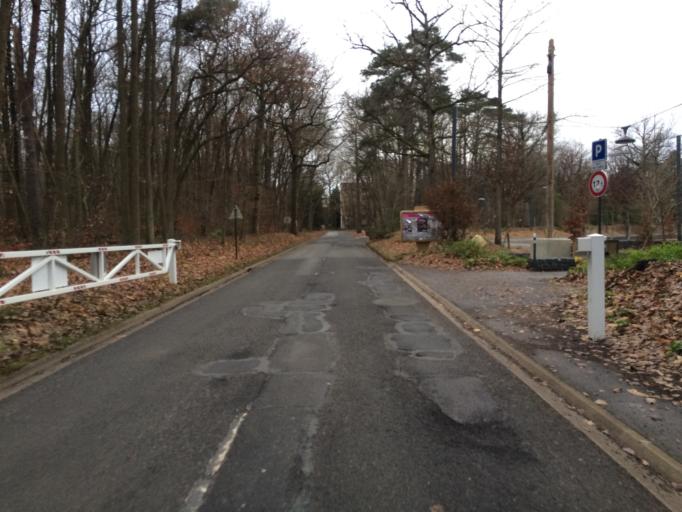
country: FR
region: Ile-de-France
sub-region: Departement de l'Essonne
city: Orsay
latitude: 48.7060
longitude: 2.1825
